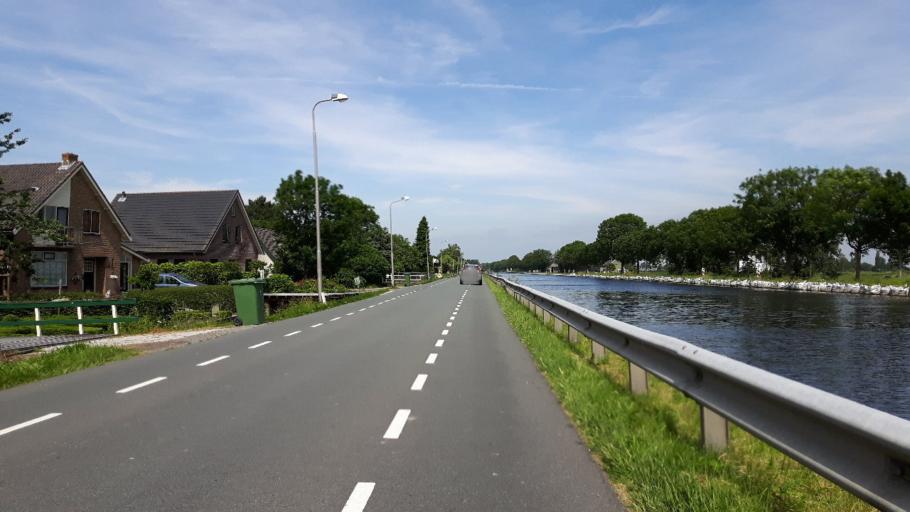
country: NL
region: South Holland
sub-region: Gemeente Nieuwkoop
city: Nieuwkoop
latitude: 52.1857
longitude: 4.7307
